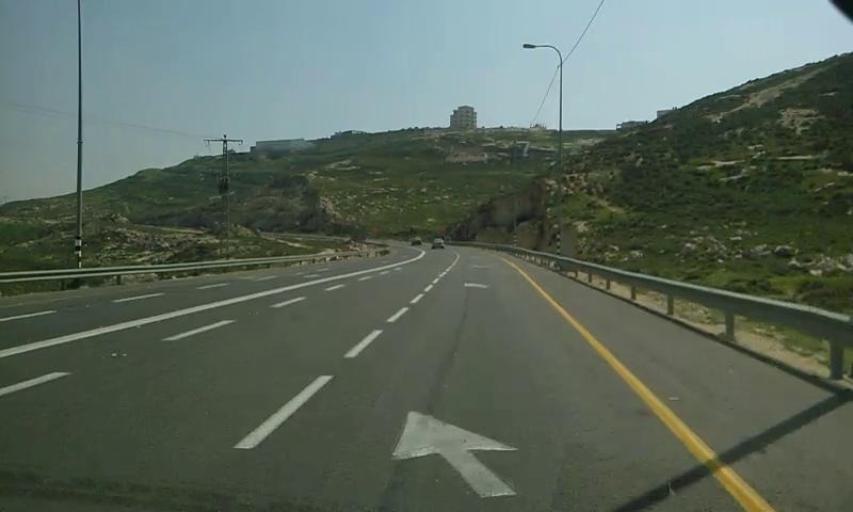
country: PS
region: West Bank
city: Jaba`
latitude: 31.8630
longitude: 35.2601
